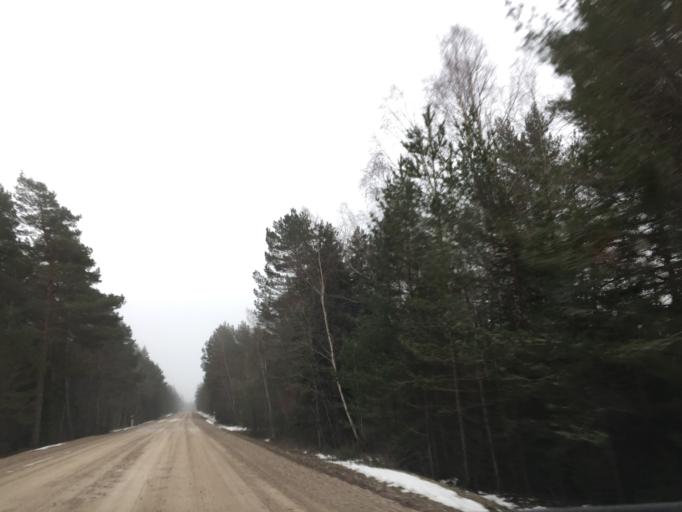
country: EE
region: Saare
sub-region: Kuressaare linn
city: Kuressaare
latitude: 58.4830
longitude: 21.9977
